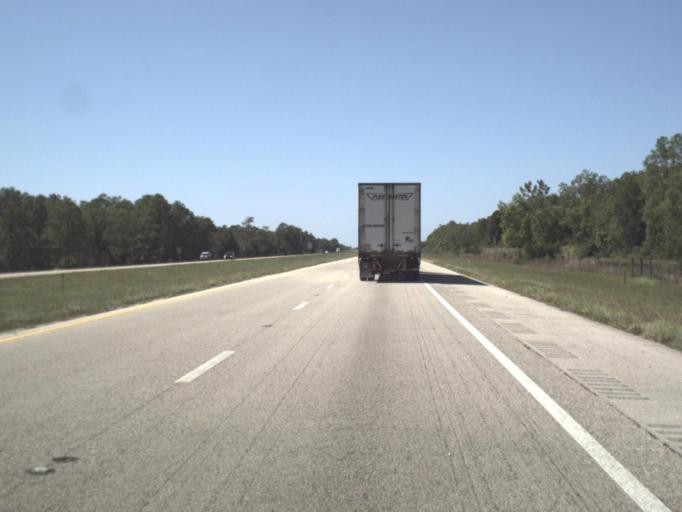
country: US
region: Florida
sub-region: Collier County
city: Golden Gate
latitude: 26.1551
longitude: -81.6499
